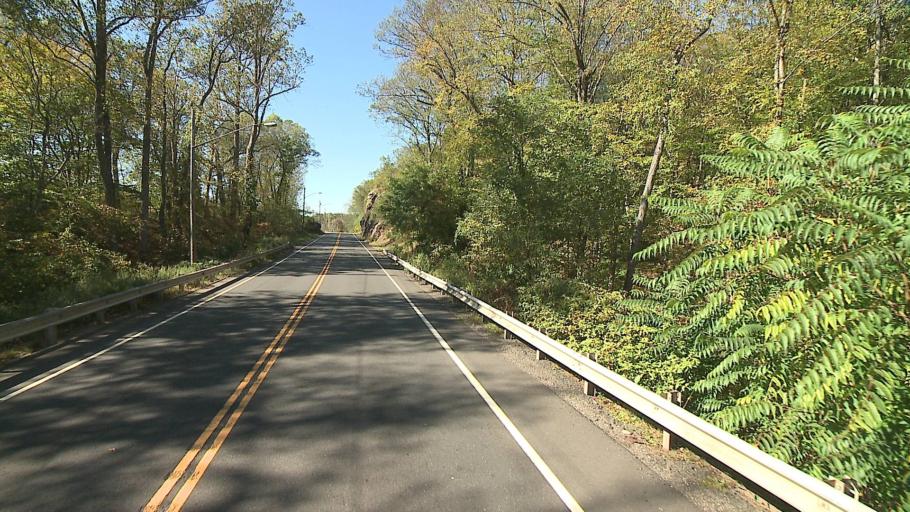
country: US
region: Connecticut
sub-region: Middlesex County
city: Portland
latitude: 41.5616
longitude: -72.5766
